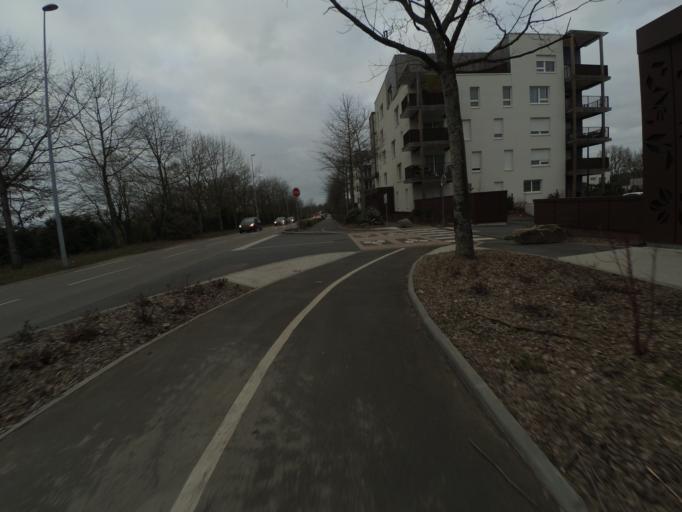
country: FR
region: Pays de la Loire
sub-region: Departement de la Loire-Atlantique
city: Carquefou
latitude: 47.2894
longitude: -1.4846
